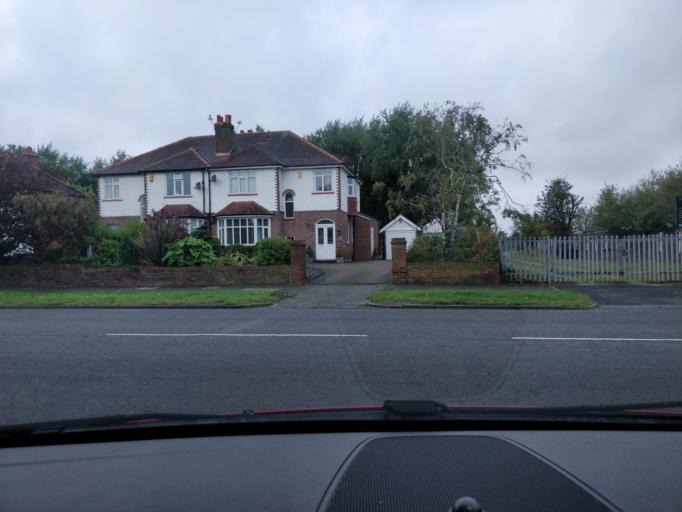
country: GB
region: England
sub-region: Sefton
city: Southport
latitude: 53.6102
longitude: -3.0226
